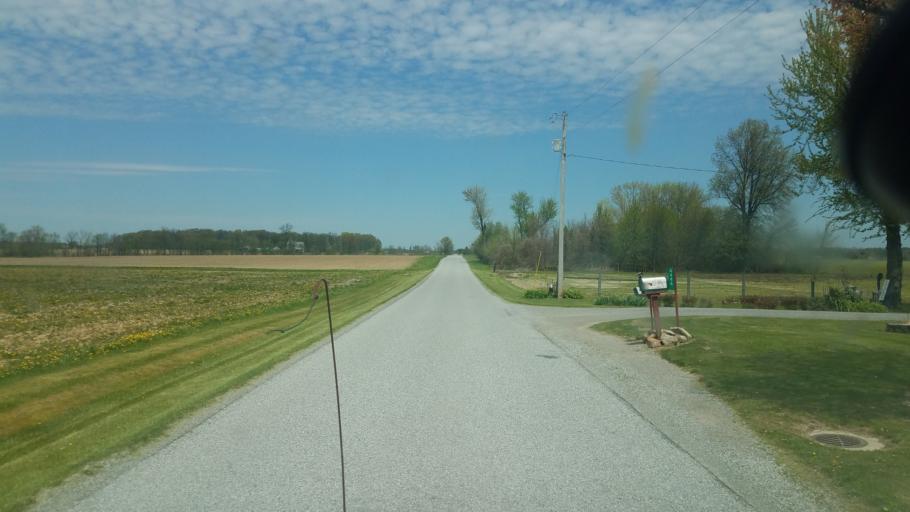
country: US
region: Ohio
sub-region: Hardin County
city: Ada
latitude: 40.8041
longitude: -83.8990
